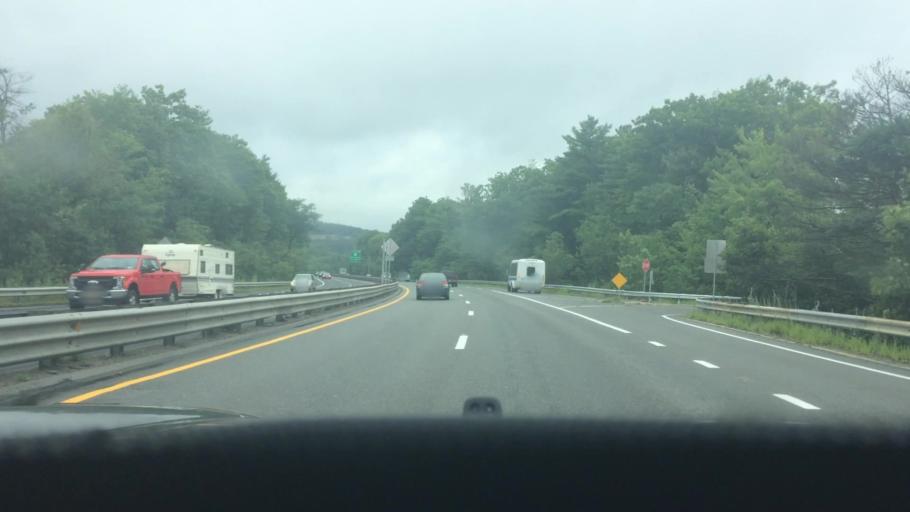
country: US
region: Massachusetts
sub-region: Worcester County
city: Fitchburg
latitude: 42.5494
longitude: -71.8310
